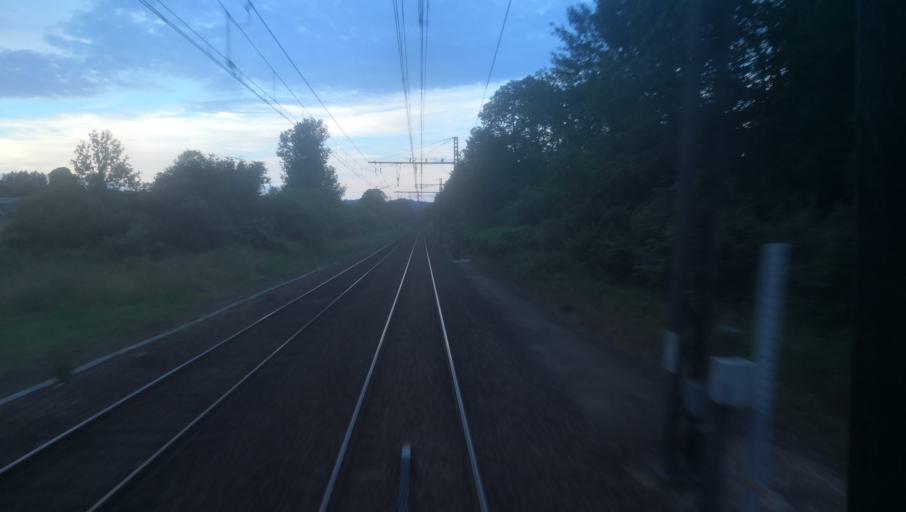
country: FR
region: Limousin
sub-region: Departement de la Haute-Vienne
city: Ambazac
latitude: 45.9947
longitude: 1.4815
